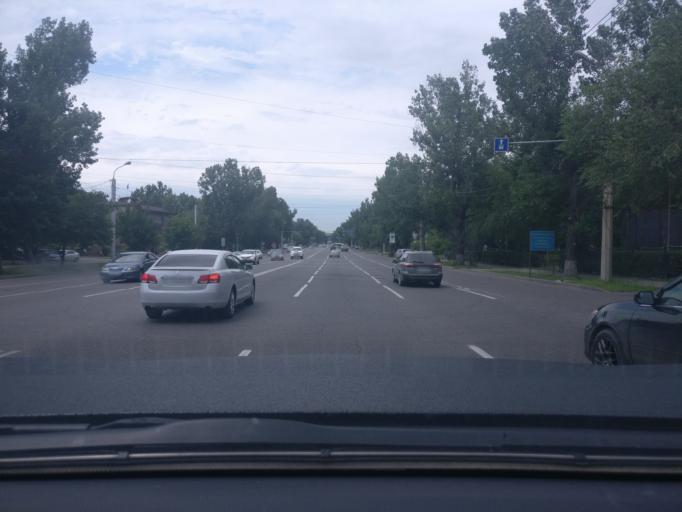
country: KZ
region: Almaty Qalasy
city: Almaty
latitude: 43.2417
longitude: 76.8581
